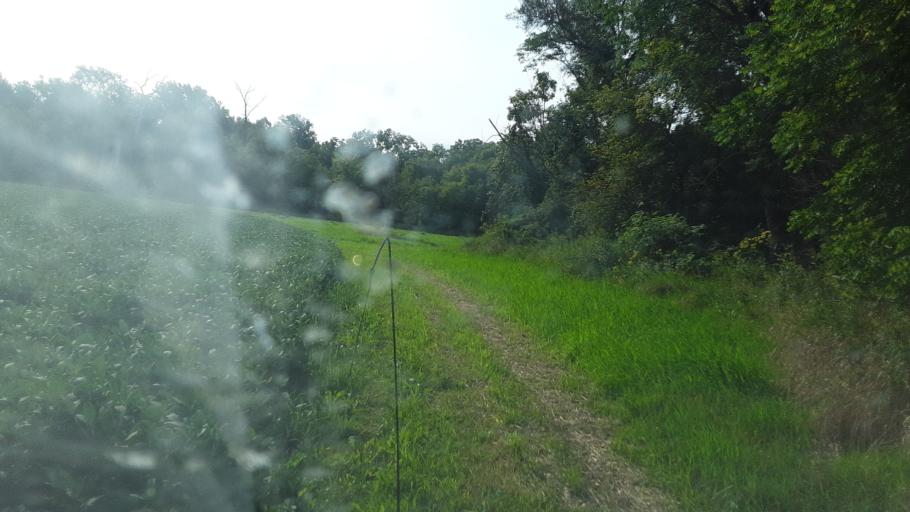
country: US
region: Ohio
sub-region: Crawford County
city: Bucyrus
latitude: 40.6599
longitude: -82.9554
